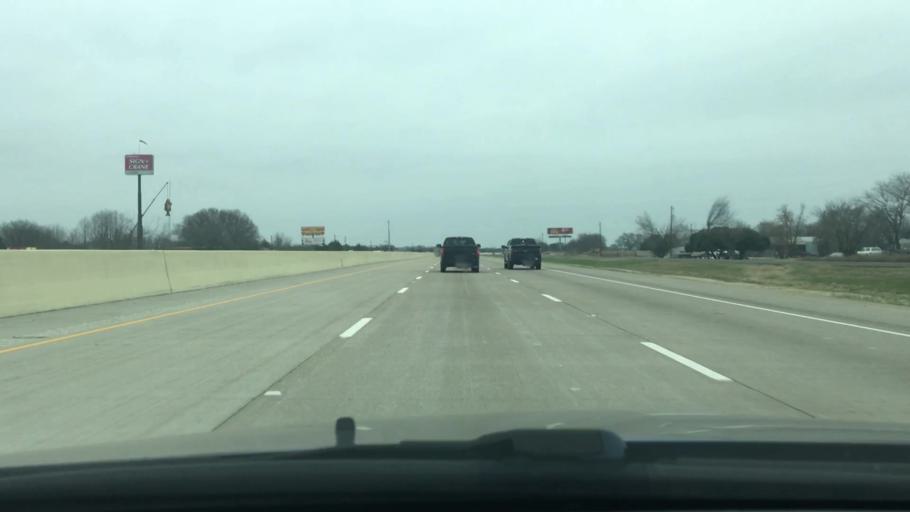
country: US
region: Texas
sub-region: Navarro County
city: Corsicana
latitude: 31.9908
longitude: -96.4266
